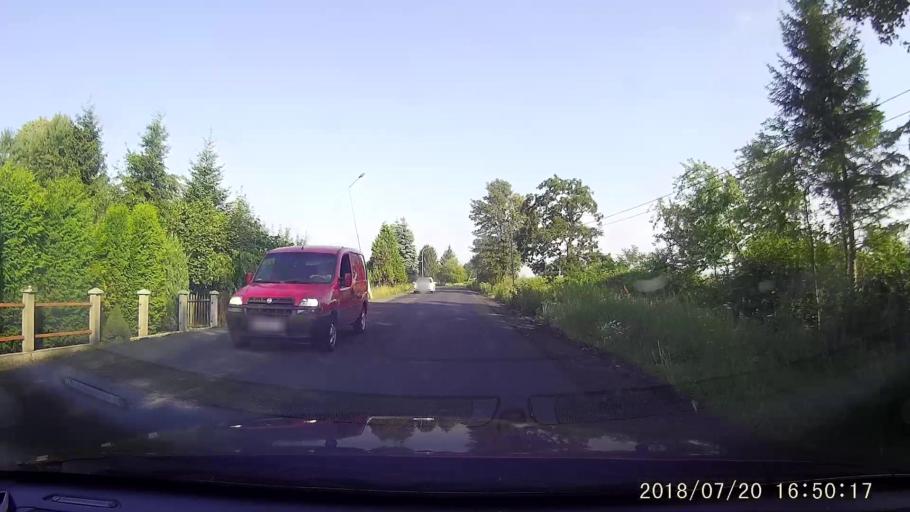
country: PL
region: Lower Silesian Voivodeship
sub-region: Powiat lubanski
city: Lesna
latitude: 51.0433
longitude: 15.2060
